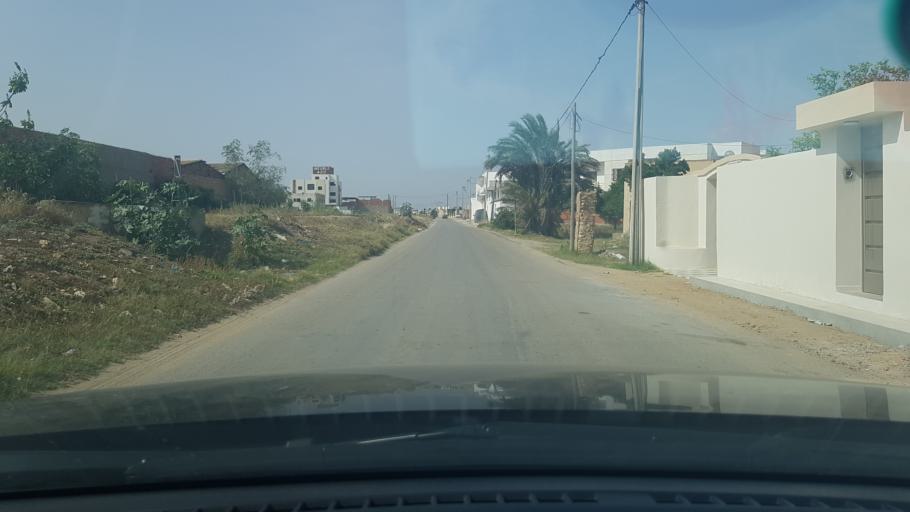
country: TN
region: Safaqis
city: Al Qarmadah
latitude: 34.8237
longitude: 10.7640
